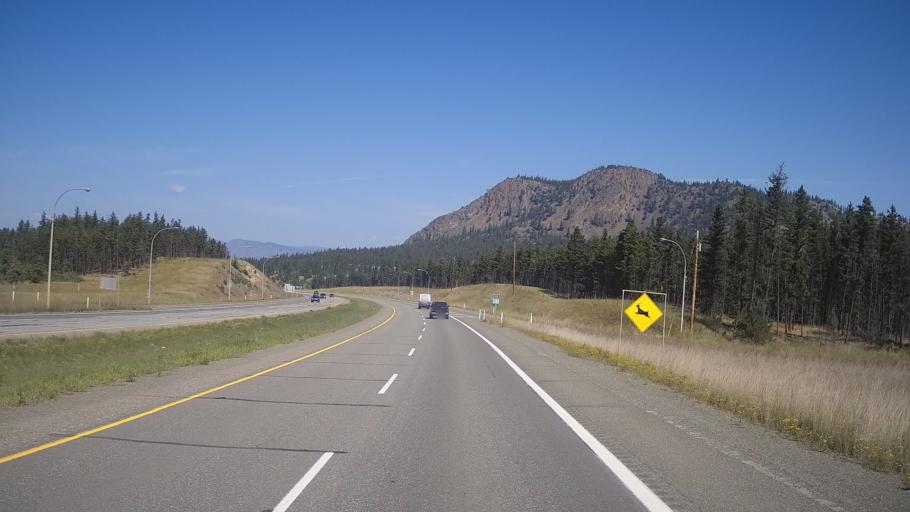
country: CA
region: British Columbia
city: Kamloops
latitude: 50.6208
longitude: -120.4719
